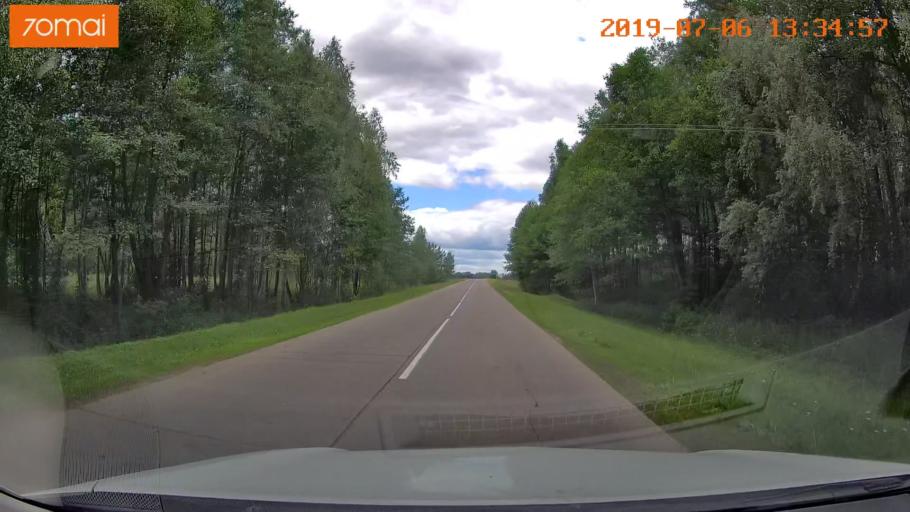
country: BY
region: Minsk
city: Enyerhyetykaw
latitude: 53.6784
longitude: 26.8893
